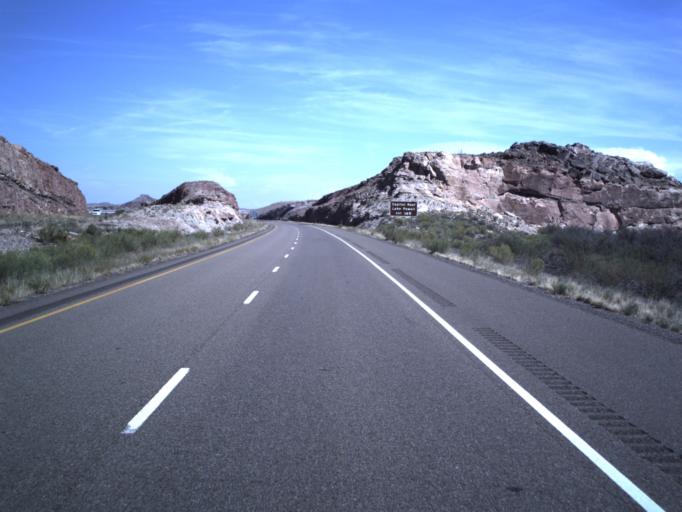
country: US
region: Utah
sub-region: Carbon County
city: East Carbon City
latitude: 38.9211
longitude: -110.3917
